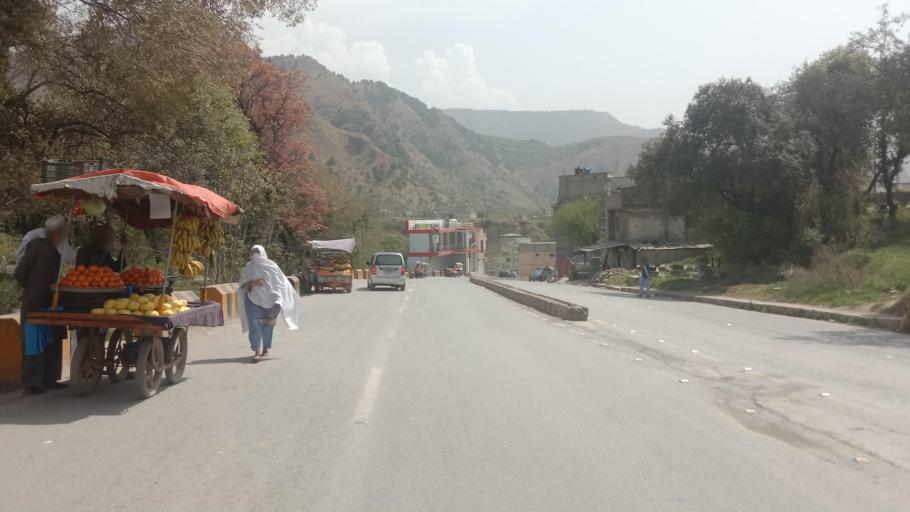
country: PK
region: Khyber Pakhtunkhwa
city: Abbottabad
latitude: 34.1576
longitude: 73.2651
